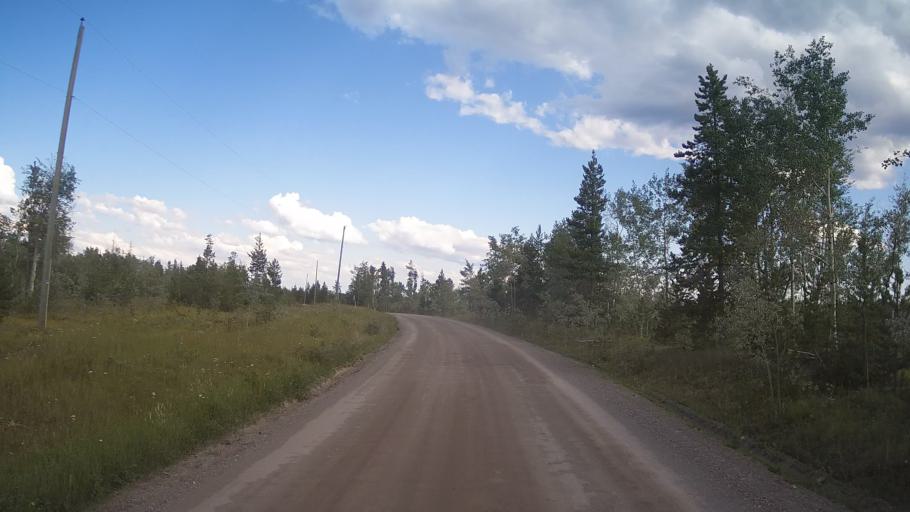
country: CA
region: British Columbia
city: Cache Creek
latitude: 51.2524
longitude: -121.6735
